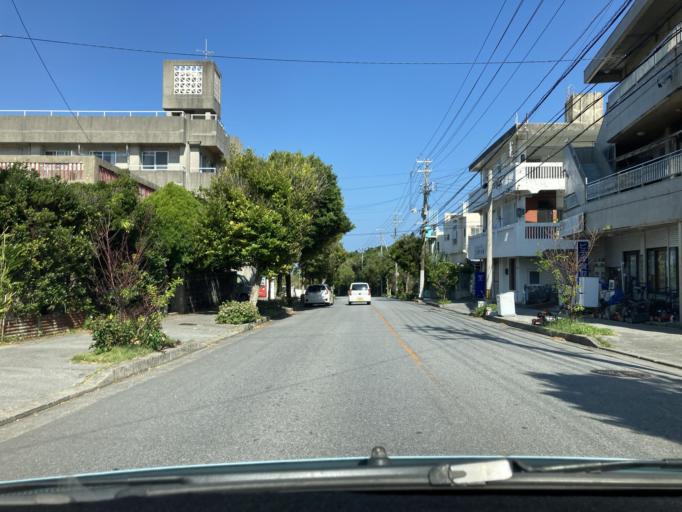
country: JP
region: Okinawa
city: Ginowan
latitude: 26.2509
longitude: 127.7261
